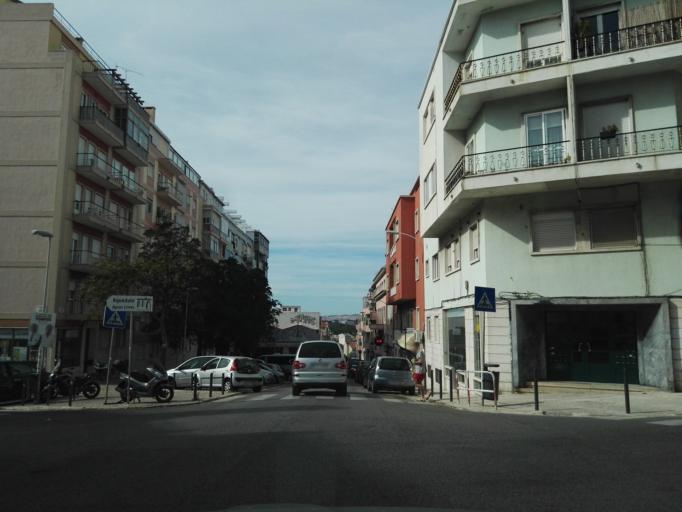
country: PT
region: Lisbon
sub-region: Lisbon
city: Lisbon
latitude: 38.7266
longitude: -9.1651
